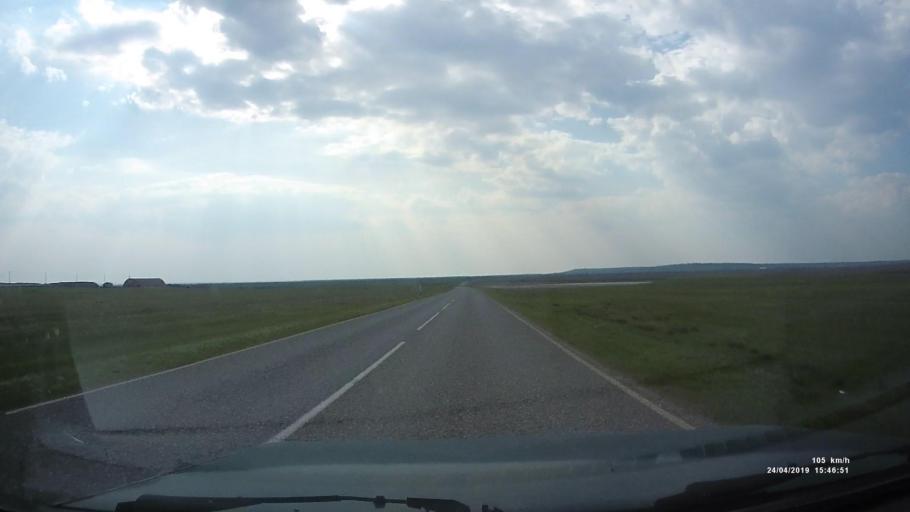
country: RU
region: Kalmykiya
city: Yashalta
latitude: 46.5935
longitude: 42.7052
